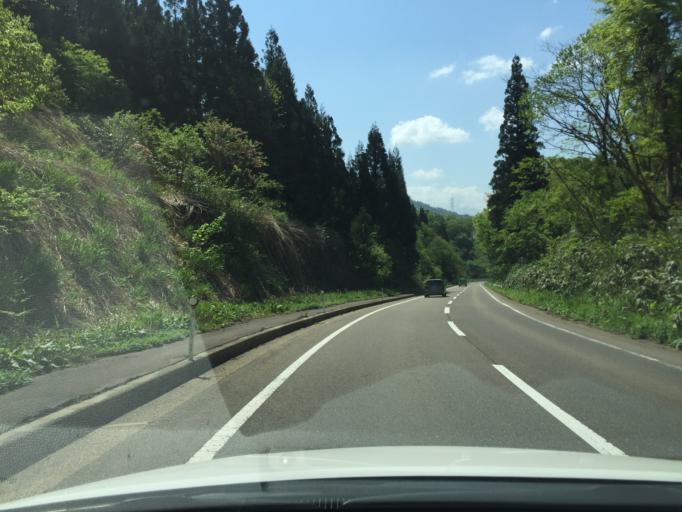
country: JP
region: Niigata
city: Kamo
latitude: 37.5833
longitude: 139.0930
